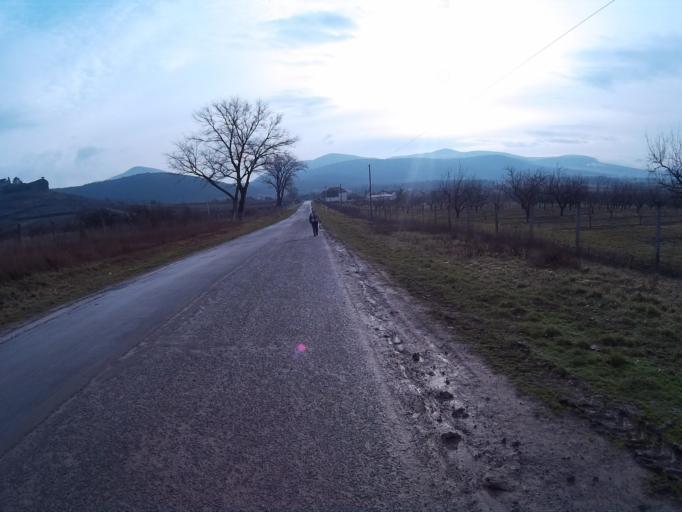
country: HU
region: Borsod-Abauj-Zemplen
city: Abaujszanto
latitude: 48.3411
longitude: 21.2234
